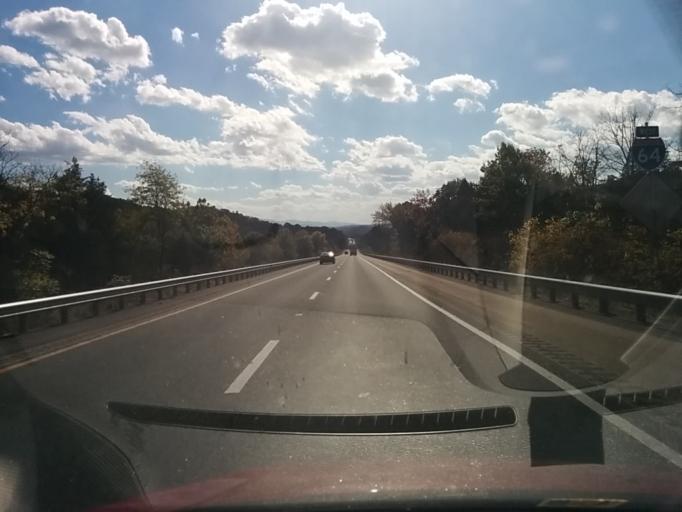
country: US
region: Virginia
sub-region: Rockbridge County
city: East Lexington
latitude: 37.8265
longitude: -79.3761
